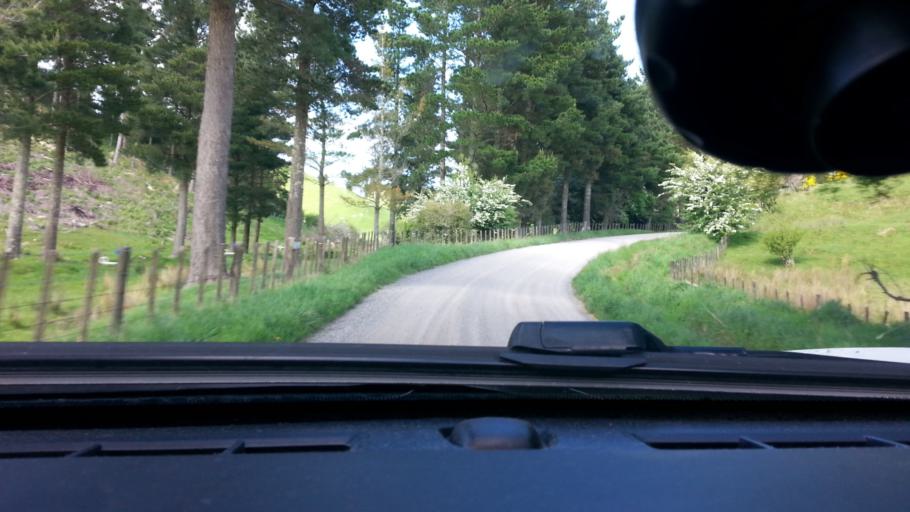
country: NZ
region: Wellington
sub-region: Masterton District
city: Masterton
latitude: -40.7453
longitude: 175.6857
